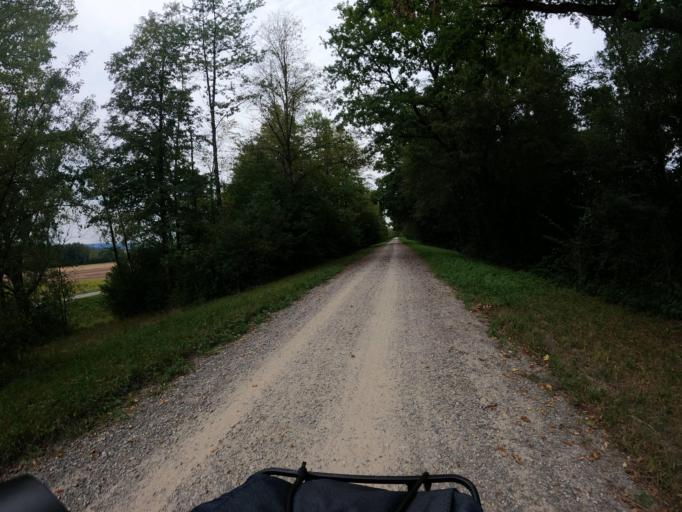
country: CH
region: Zurich
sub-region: Bezirk Affoltern
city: Ottenbach
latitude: 47.2718
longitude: 8.3996
